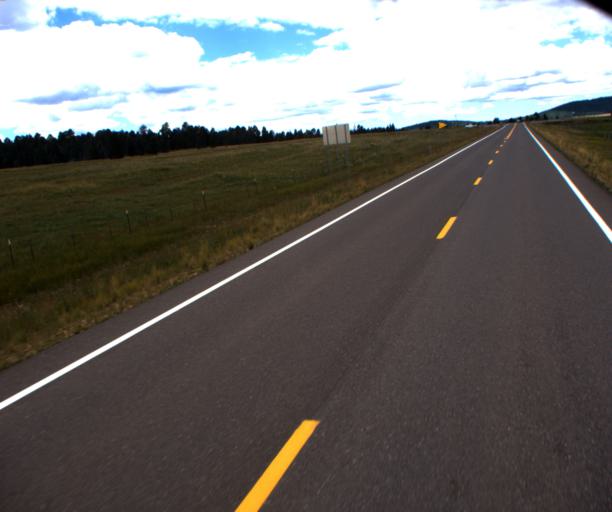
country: US
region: Arizona
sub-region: Apache County
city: Eagar
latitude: 33.9987
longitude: -109.5252
